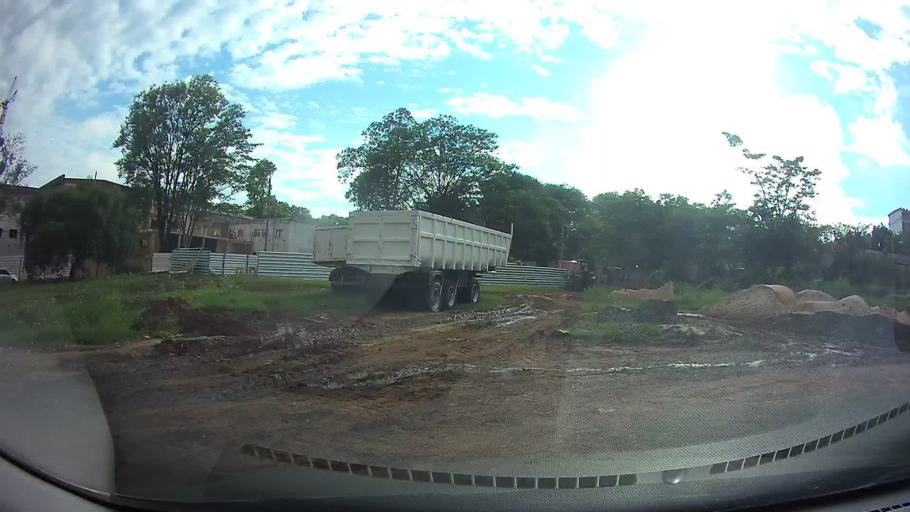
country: PY
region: Asuncion
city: Asuncion
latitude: -25.2705
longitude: -57.5821
